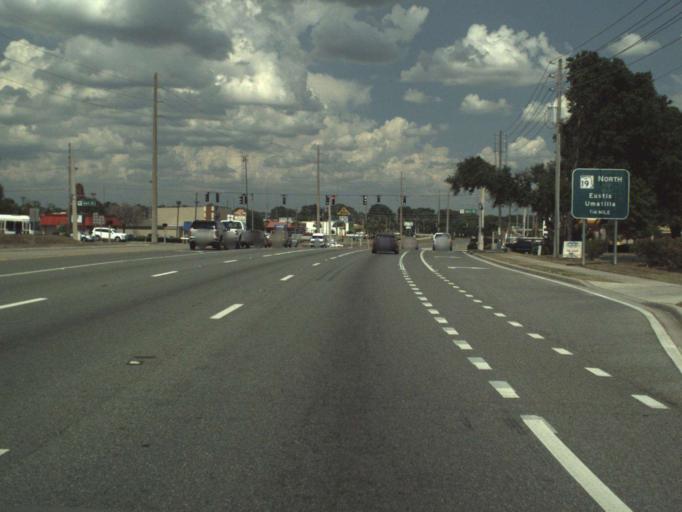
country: US
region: Florida
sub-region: Lake County
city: Eustis
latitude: 28.8228
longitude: -81.6929
